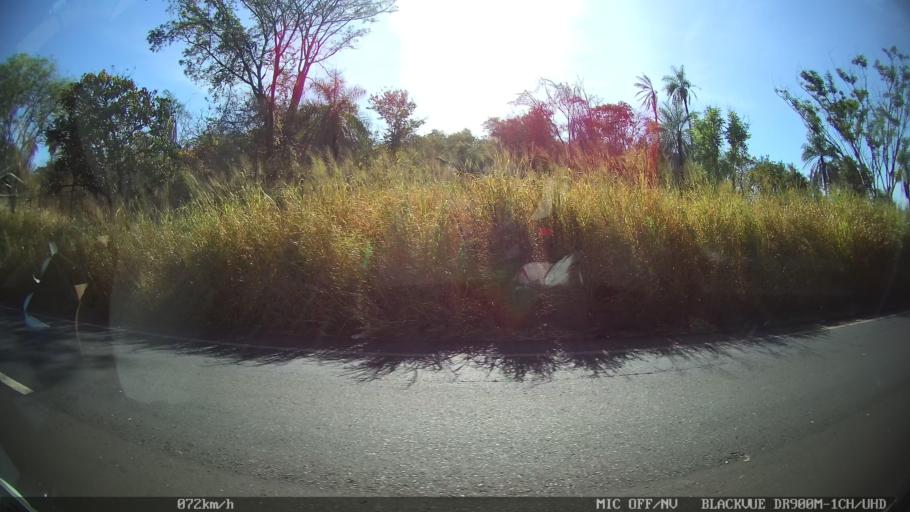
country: BR
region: Sao Paulo
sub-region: Barretos
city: Barretos
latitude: -20.5956
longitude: -48.7172
